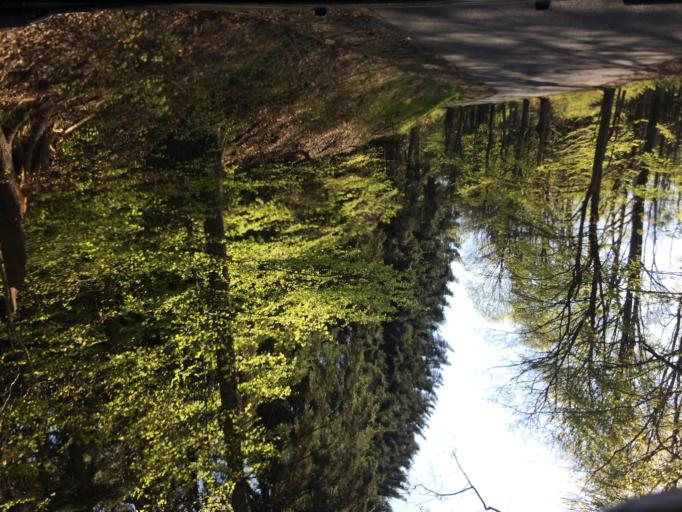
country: PL
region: Lower Silesian Voivodeship
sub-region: Powiat klodzki
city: Jugow
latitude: 50.6696
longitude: 16.5164
